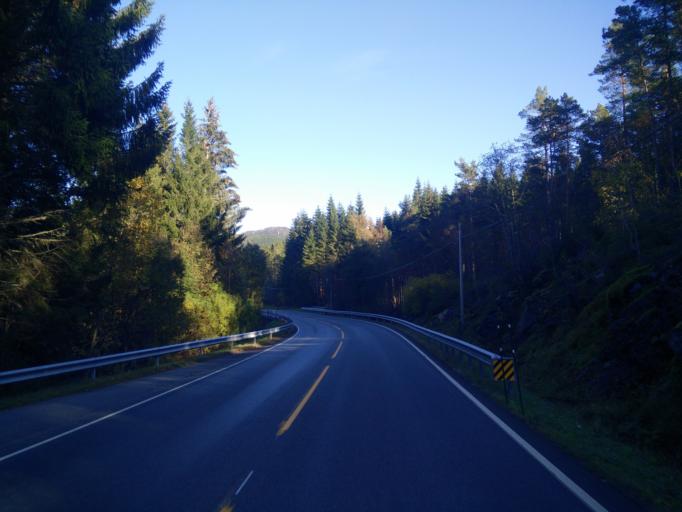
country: NO
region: More og Romsdal
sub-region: Halsa
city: Liaboen
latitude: 63.0810
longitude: 8.3368
